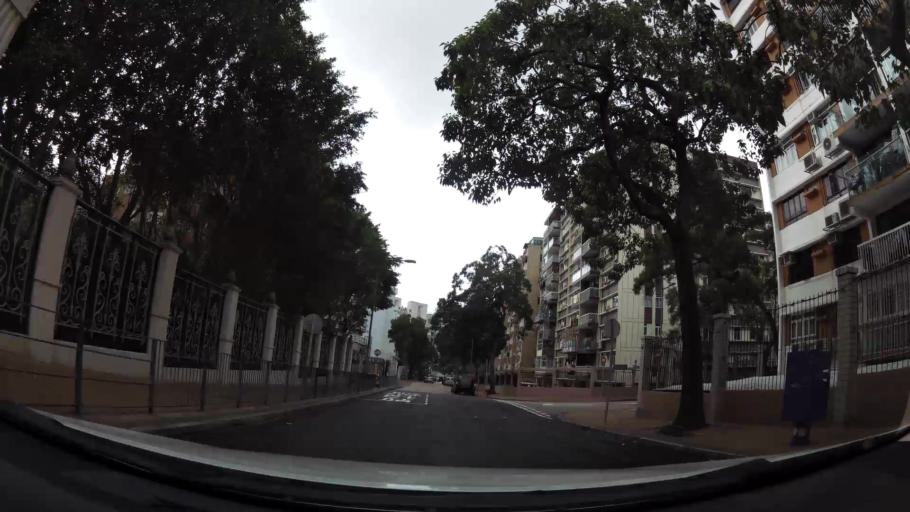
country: HK
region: Wong Tai Sin
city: Wong Tai Sin
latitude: 22.3422
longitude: 114.1834
